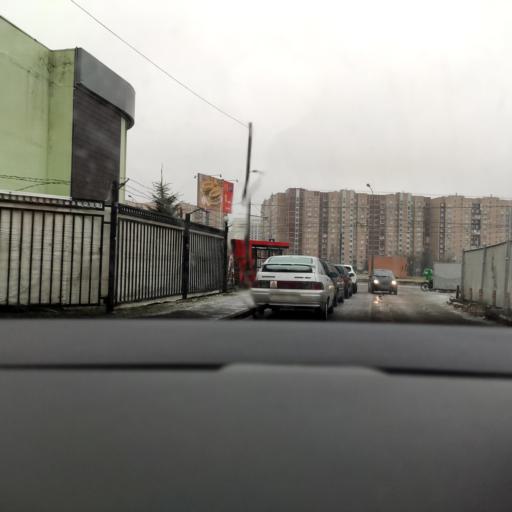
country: RU
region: Moskovskaya
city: Reutov
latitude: 55.7455
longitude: 37.8565
